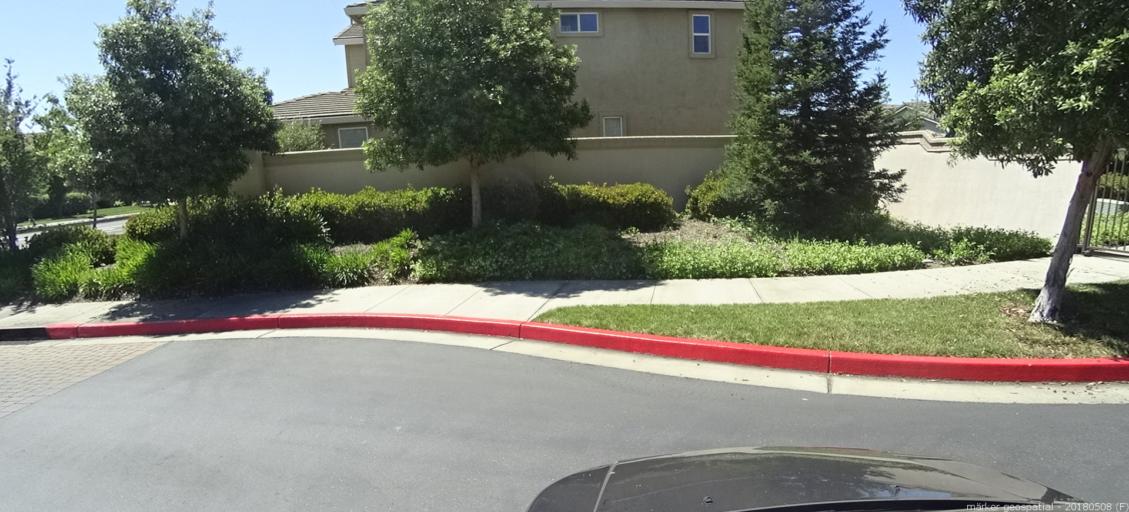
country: US
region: California
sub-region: Sacramento County
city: Elverta
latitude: 38.6802
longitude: -121.5253
